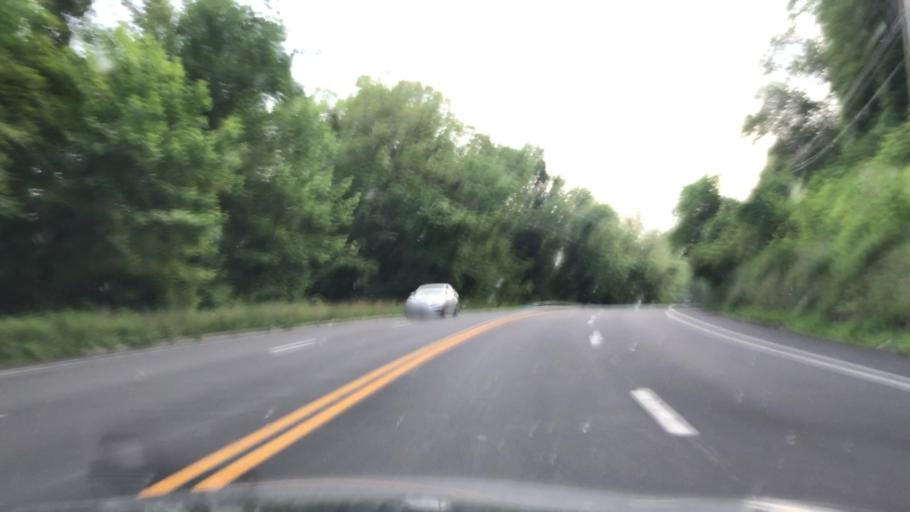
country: US
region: New York
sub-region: Orange County
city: Harriman
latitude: 41.2687
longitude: -74.1568
